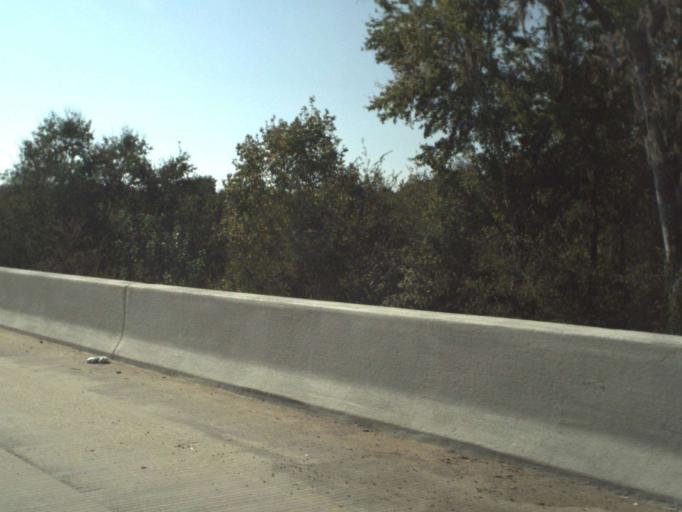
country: US
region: Florida
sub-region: Gadsden County
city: Quincy
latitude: 30.5866
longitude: -84.5519
